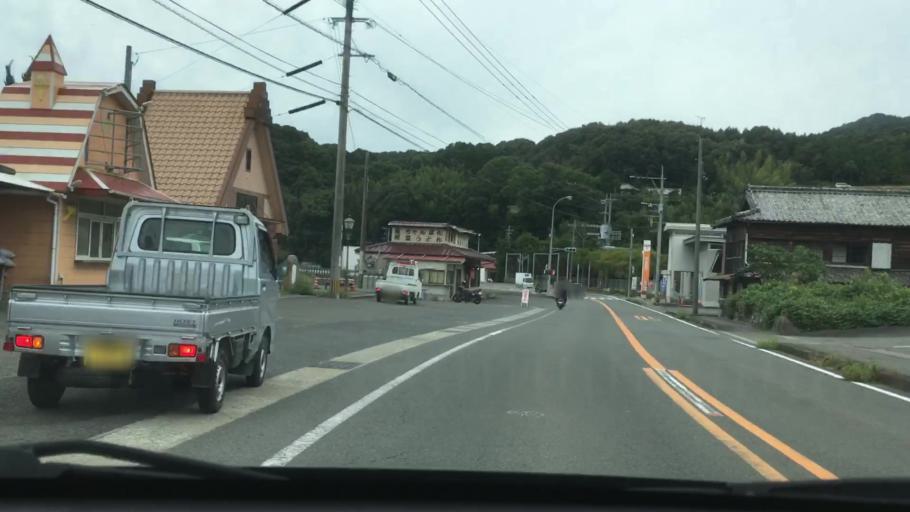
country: JP
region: Nagasaki
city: Sasebo
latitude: 33.0175
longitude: 129.7349
